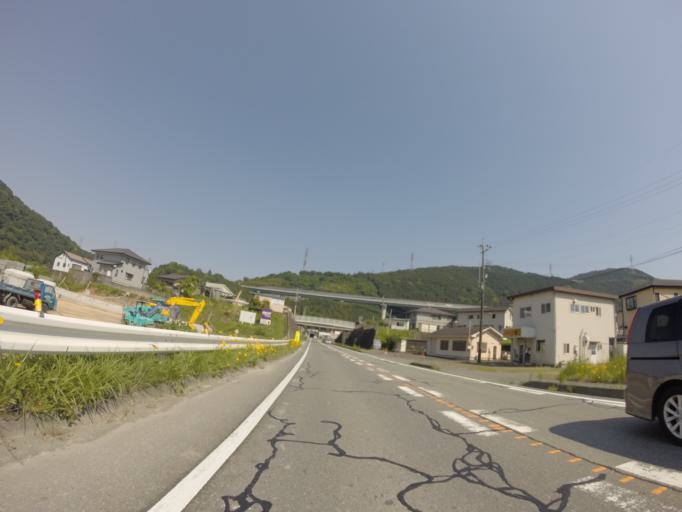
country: JP
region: Shizuoka
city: Fujinomiya
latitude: 35.1812
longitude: 138.6047
